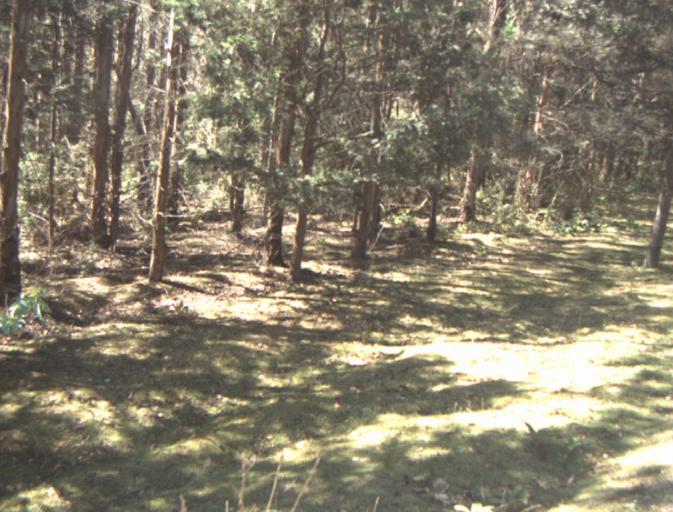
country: AU
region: Tasmania
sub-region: Dorset
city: Scottsdale
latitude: -41.2564
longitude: 147.3462
